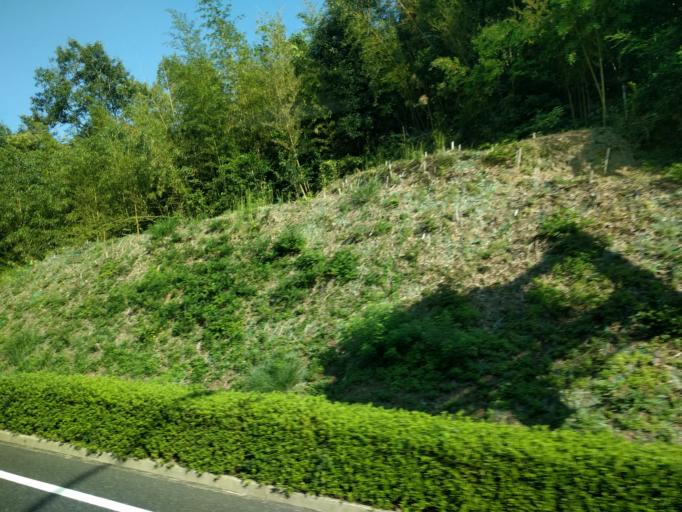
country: JP
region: Hyogo
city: Kobe
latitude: 34.6963
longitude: 135.1519
